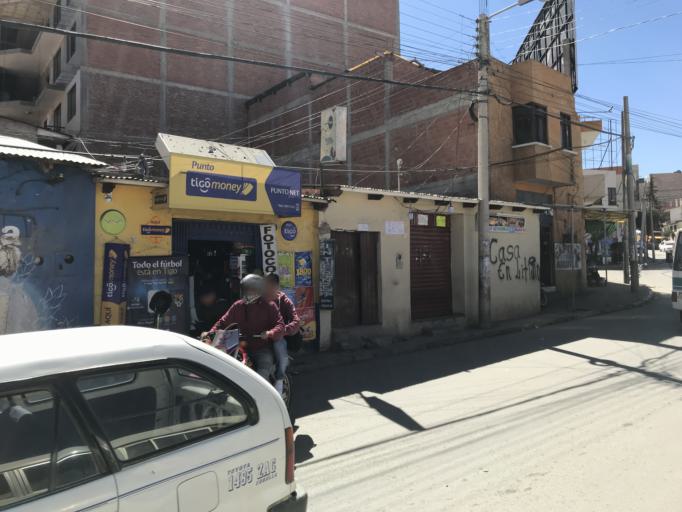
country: BO
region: Chuquisaca
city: Sucre
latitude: -19.0386
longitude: -65.2453
